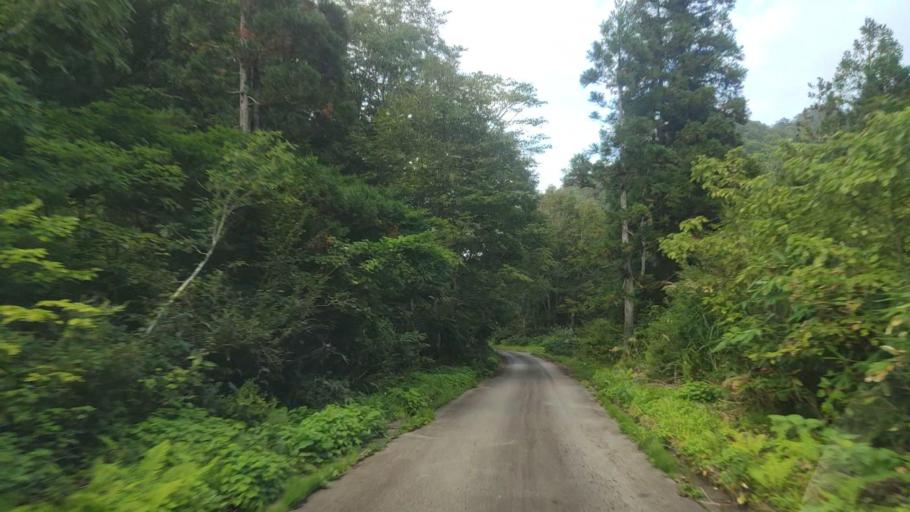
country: JP
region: Toyama
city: Yatsuomachi-higashikumisaka
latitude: 36.3563
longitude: 137.0671
